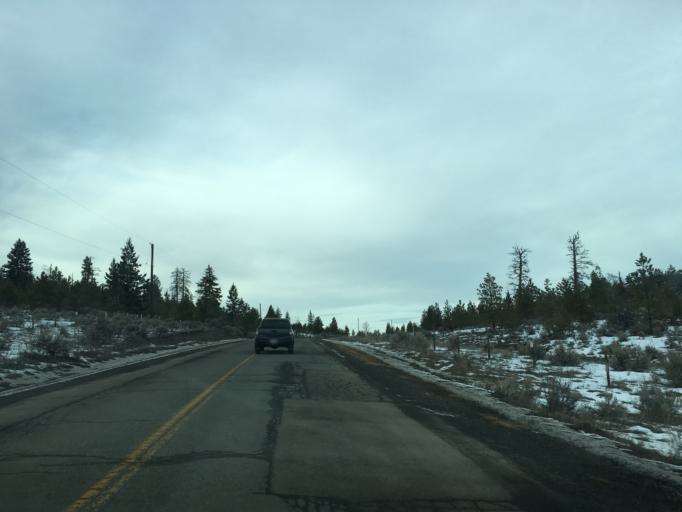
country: CA
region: British Columbia
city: Kamloops
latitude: 50.6366
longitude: -120.4480
